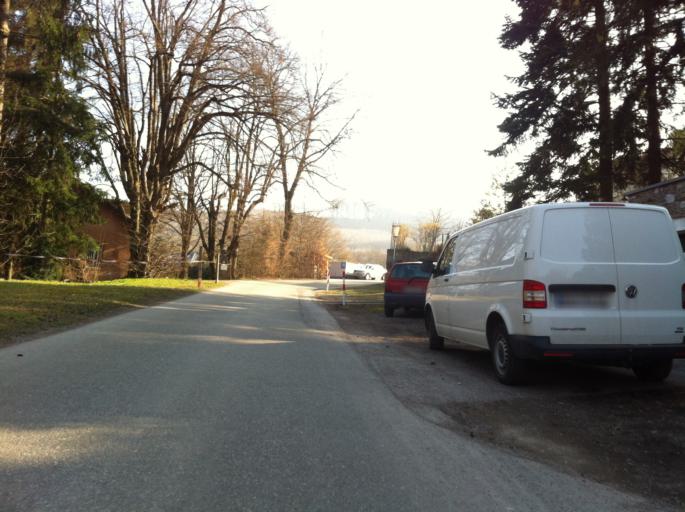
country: AT
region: Lower Austria
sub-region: Politischer Bezirk Wien-Umgebung
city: Wolfsgraben
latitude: 48.1810
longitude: 16.1121
